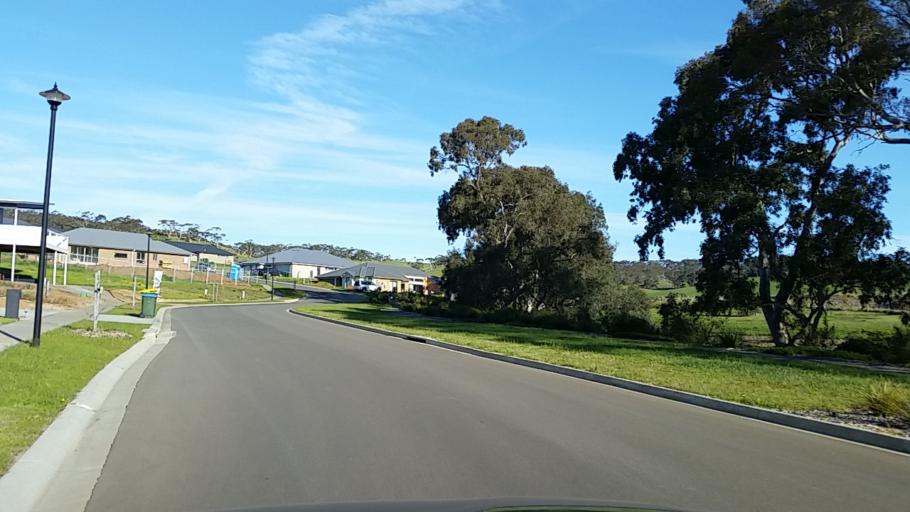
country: AU
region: South Australia
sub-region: Mount Barker
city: Meadows
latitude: -35.1848
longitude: 138.7585
